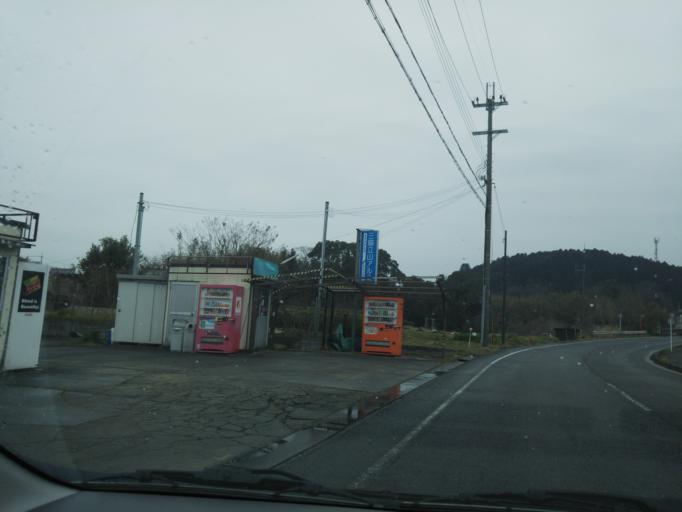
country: JP
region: Shiga Prefecture
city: Minakuchicho-matoba
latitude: 34.9596
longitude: 136.2025
